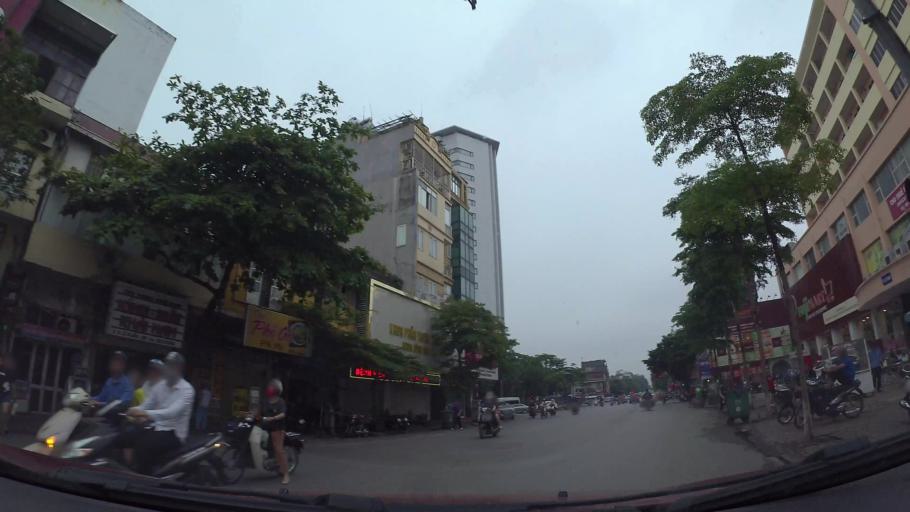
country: VN
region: Ha Noi
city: Hanoi
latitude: 21.0187
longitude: 105.8413
